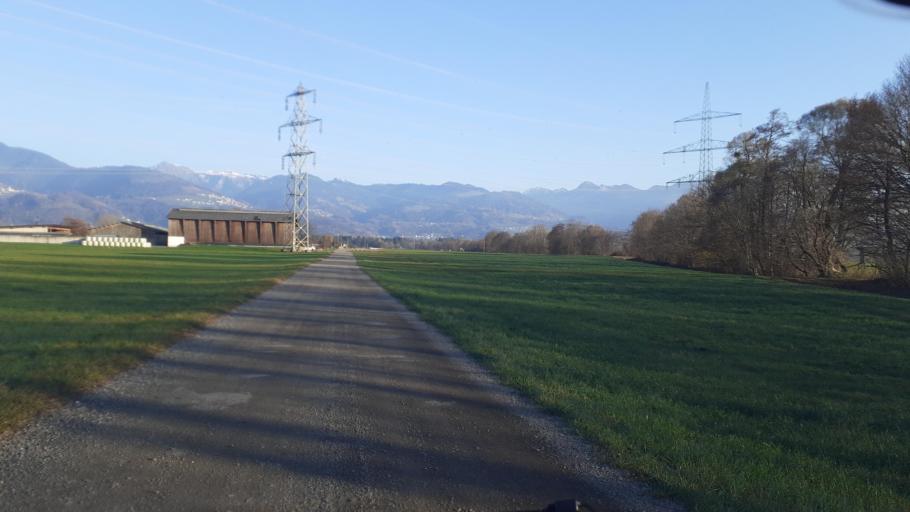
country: AT
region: Vorarlberg
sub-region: Politischer Bezirk Feldkirch
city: Meiningen
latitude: 47.3056
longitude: 9.5934
